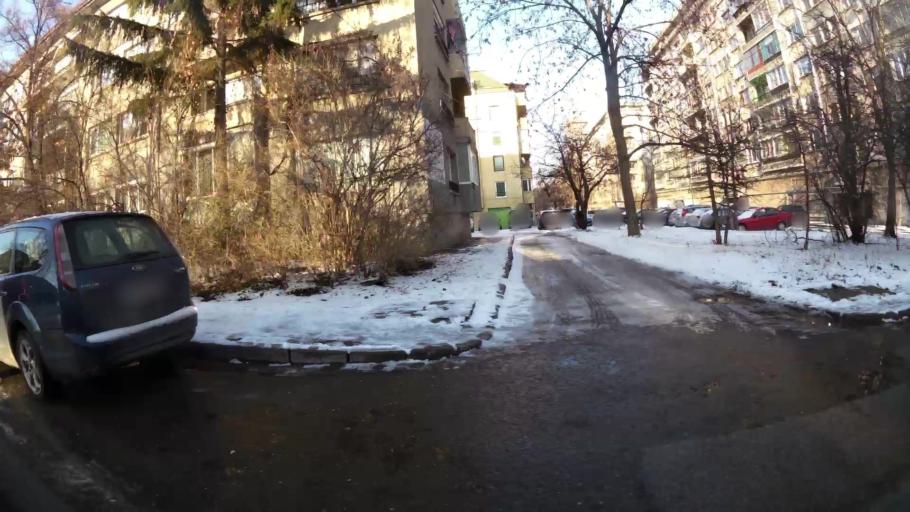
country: BG
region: Sofia-Capital
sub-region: Stolichna Obshtina
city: Sofia
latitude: 42.6773
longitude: 23.3637
